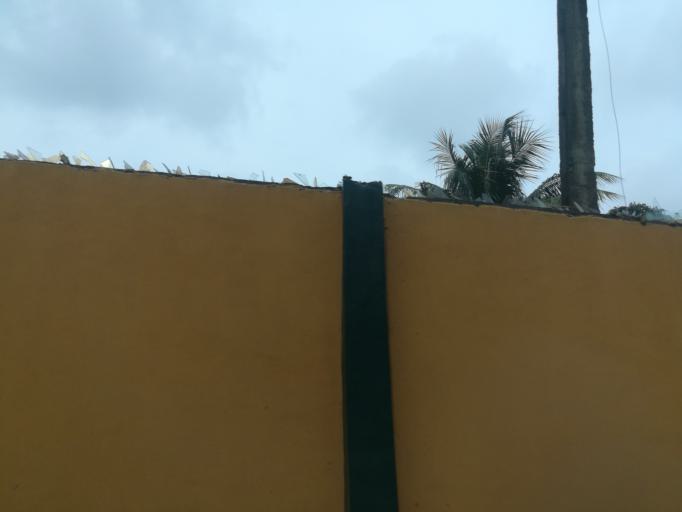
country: NG
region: Lagos
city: Ojota
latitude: 6.5668
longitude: 3.3653
